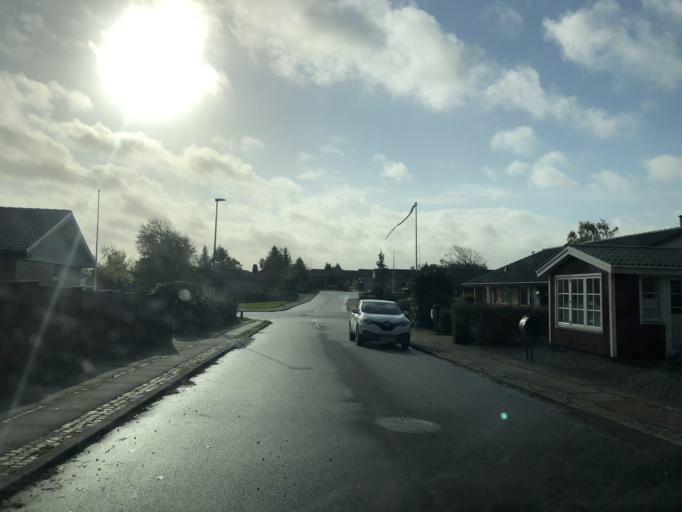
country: DK
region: South Denmark
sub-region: Billund Kommune
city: Grindsted
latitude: 55.6944
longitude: 8.9927
